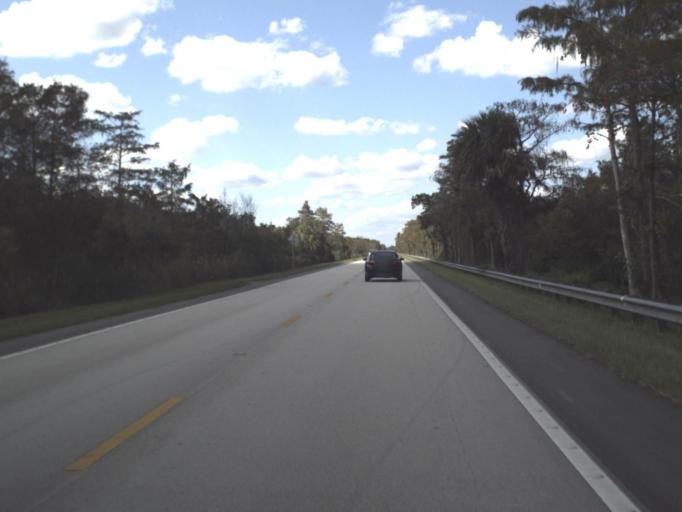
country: US
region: Florida
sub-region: Miami-Dade County
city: Kendall West
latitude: 25.8341
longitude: -80.9064
